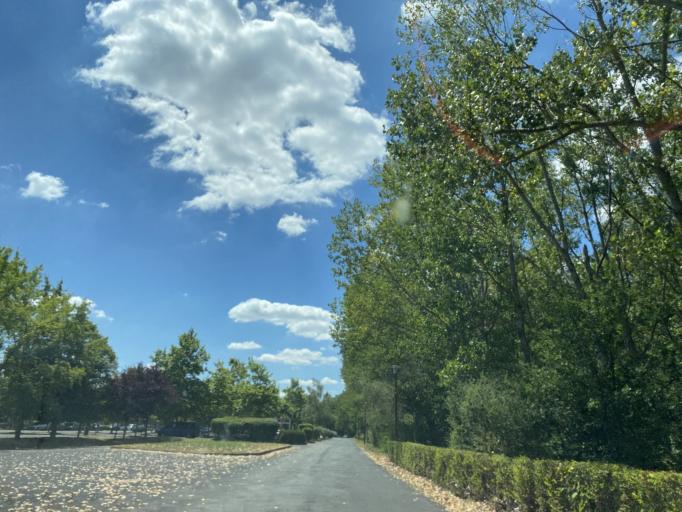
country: FR
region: Auvergne
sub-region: Departement du Puy-de-Dome
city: Peschadoires
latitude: 45.8711
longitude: 3.4841
